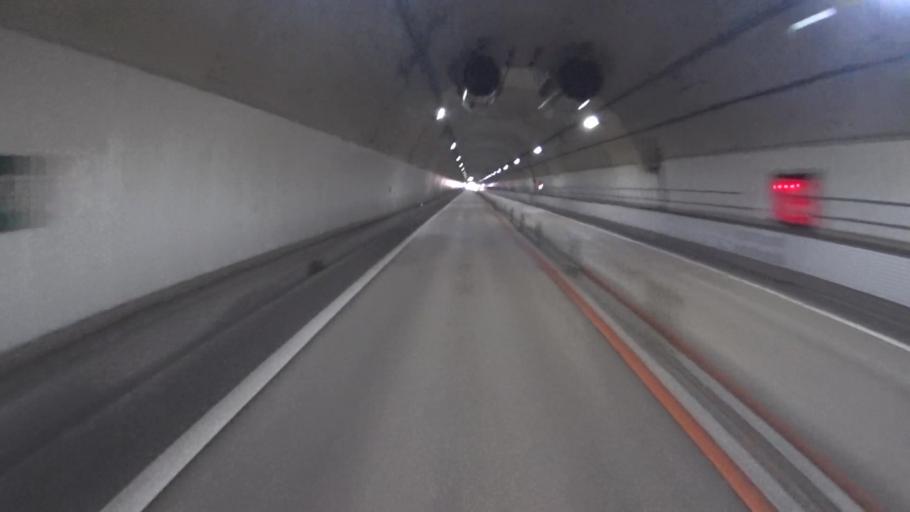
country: JP
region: Kyoto
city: Ayabe
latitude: 35.3977
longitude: 135.2342
